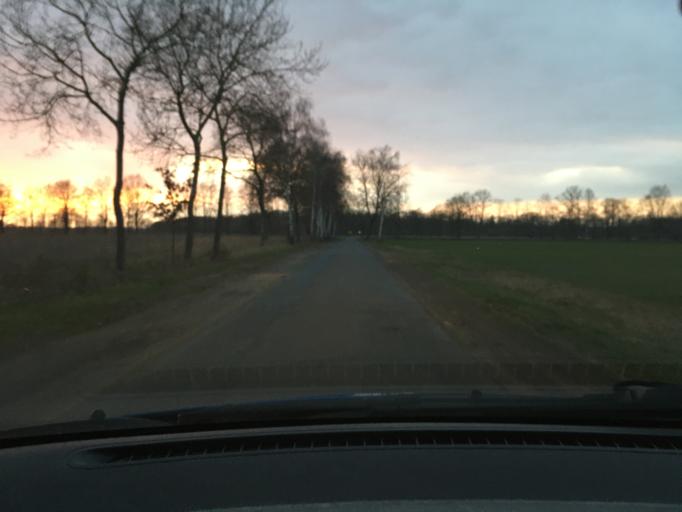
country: DE
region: Lower Saxony
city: Neetze
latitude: 53.3040
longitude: 10.6644
